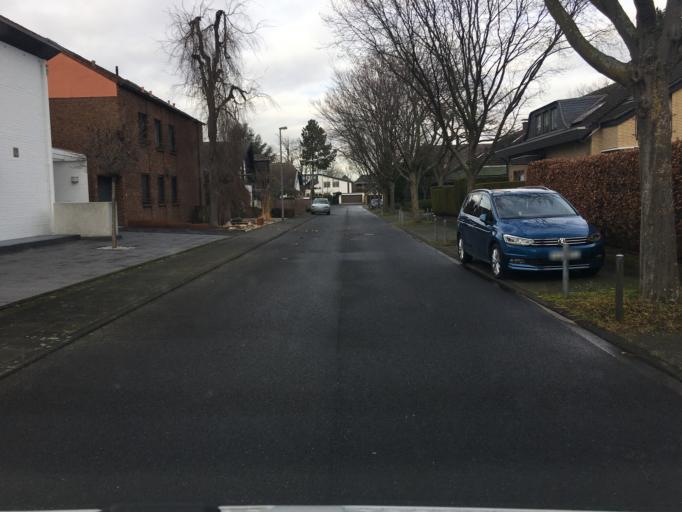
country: DE
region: North Rhine-Westphalia
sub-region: Regierungsbezirk Koln
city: Mengenich
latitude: 50.9498
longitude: 6.8610
